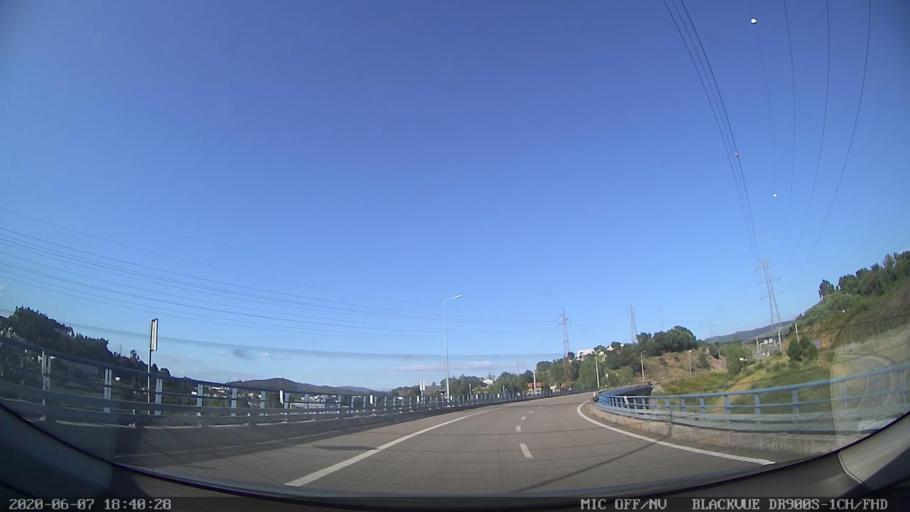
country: PT
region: Braga
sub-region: Guimaraes
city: Selho
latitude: 41.4296
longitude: -8.3389
